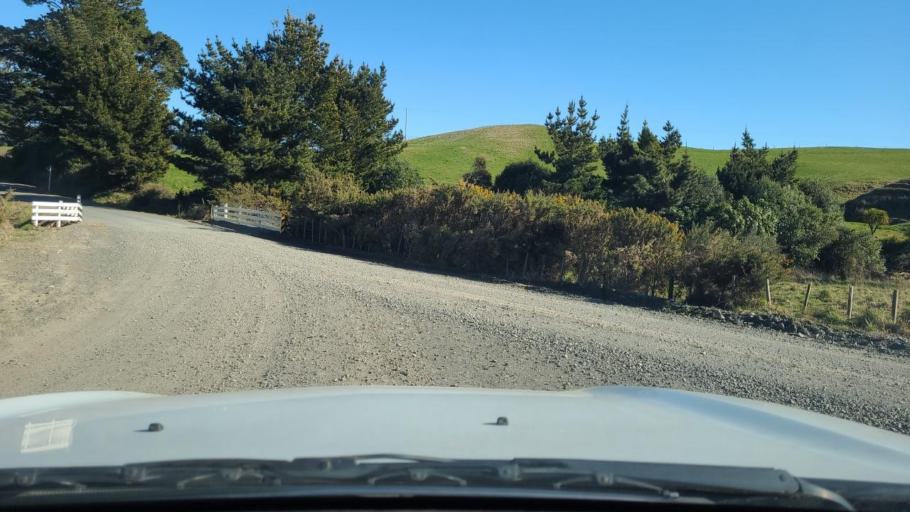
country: NZ
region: Hawke's Bay
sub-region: Napier City
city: Taradale
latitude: -39.3492
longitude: 176.5392
